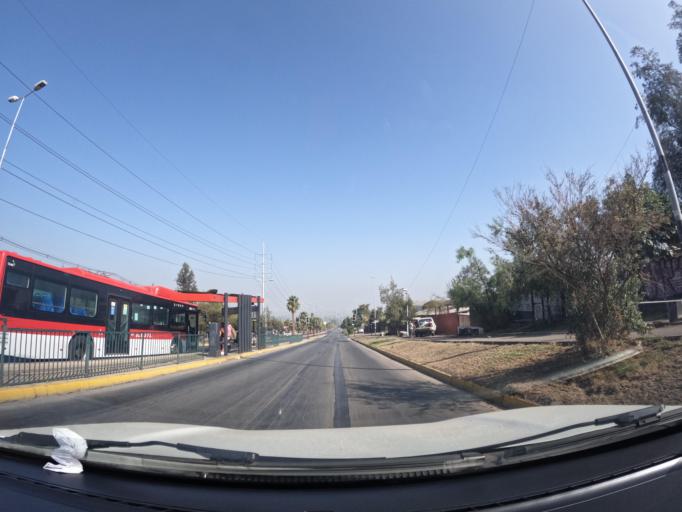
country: CL
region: Santiago Metropolitan
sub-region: Provincia de Santiago
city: Villa Presidente Frei, Nunoa, Santiago, Chile
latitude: -33.4789
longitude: -70.5276
